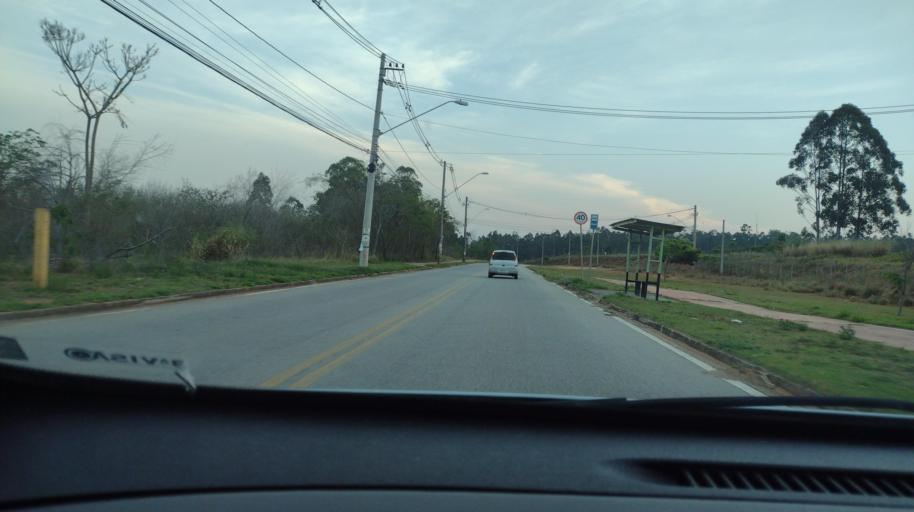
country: BR
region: Sao Paulo
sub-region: Sorocaba
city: Sorocaba
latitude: -23.3732
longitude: -47.4738
